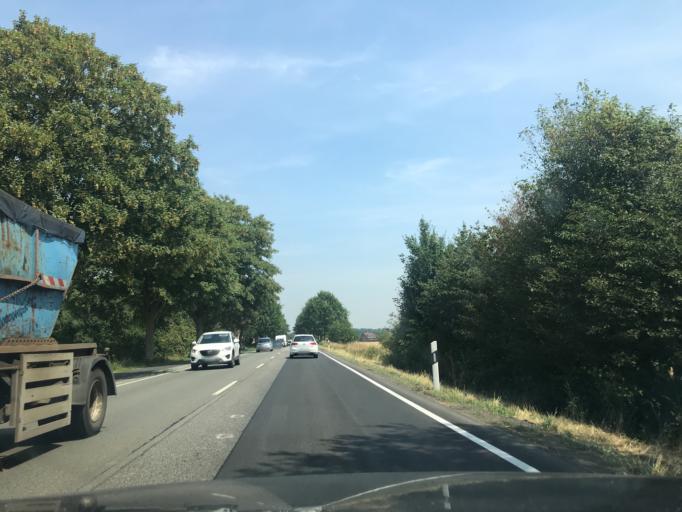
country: DE
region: North Rhine-Westphalia
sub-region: Regierungsbezirk Dusseldorf
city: Alpen
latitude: 51.6100
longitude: 6.5566
